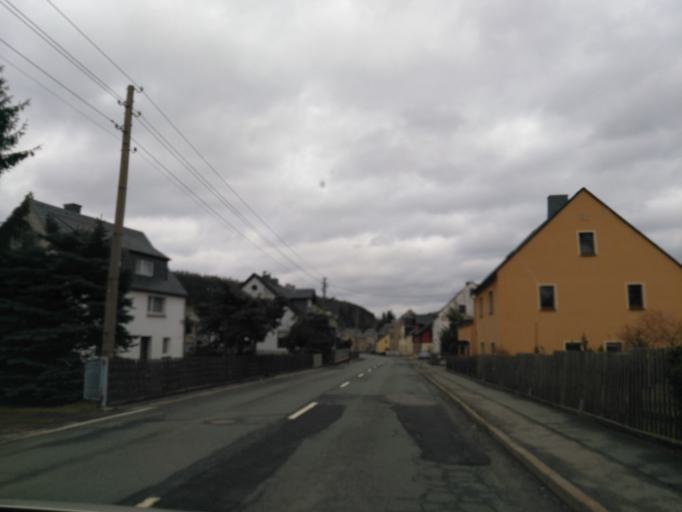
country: DE
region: Saxony
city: Thum
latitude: 50.6740
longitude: 12.9751
